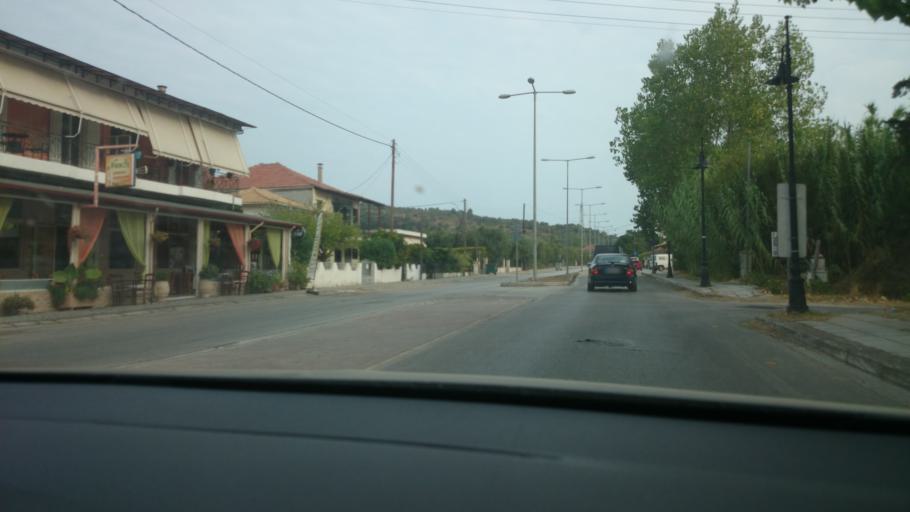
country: GR
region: Ionian Islands
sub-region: Lefkada
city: Lefkada
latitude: 38.8001
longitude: 20.7160
